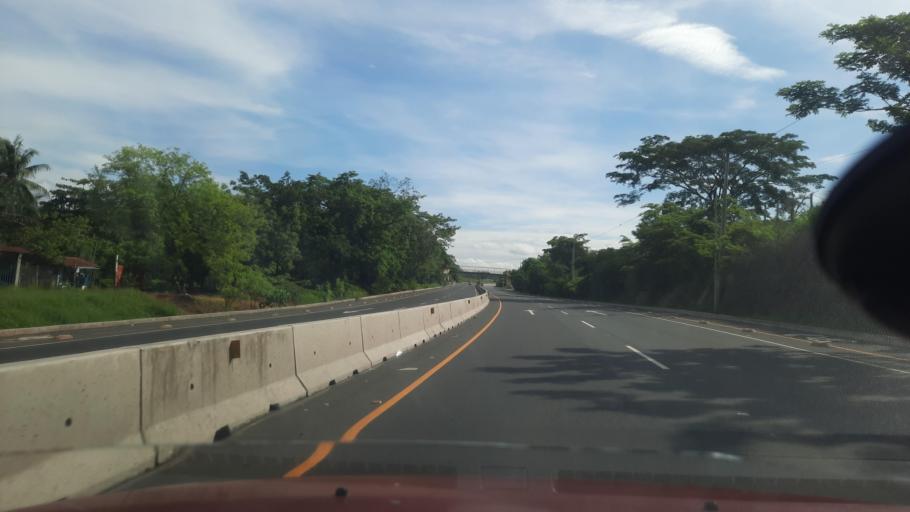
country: SV
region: La Paz
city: El Rosario
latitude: 13.4682
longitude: -89.0043
